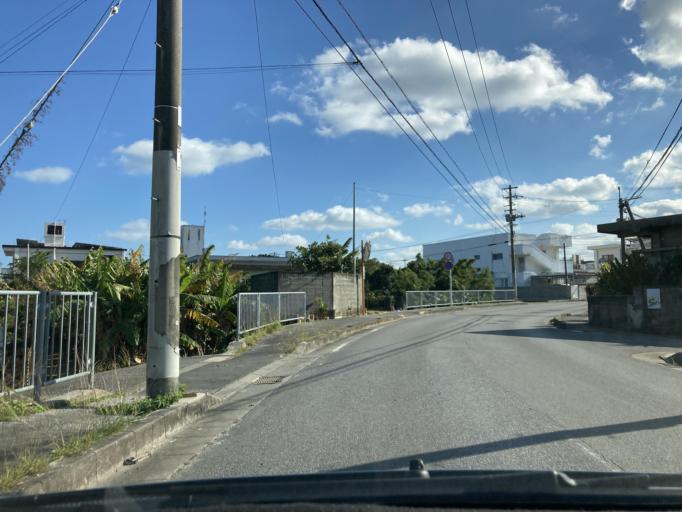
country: JP
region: Okinawa
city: Katsuren-haebaru
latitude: 26.3132
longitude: 127.9104
